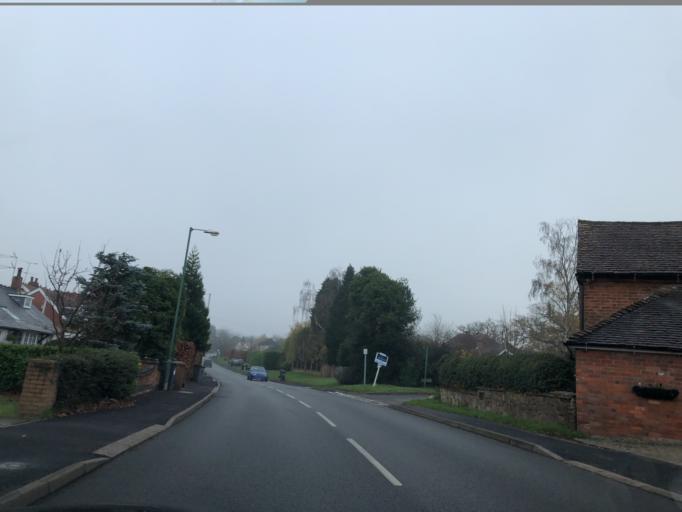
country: GB
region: England
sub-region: Solihull
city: Balsall Common
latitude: 52.3862
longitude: -1.6599
